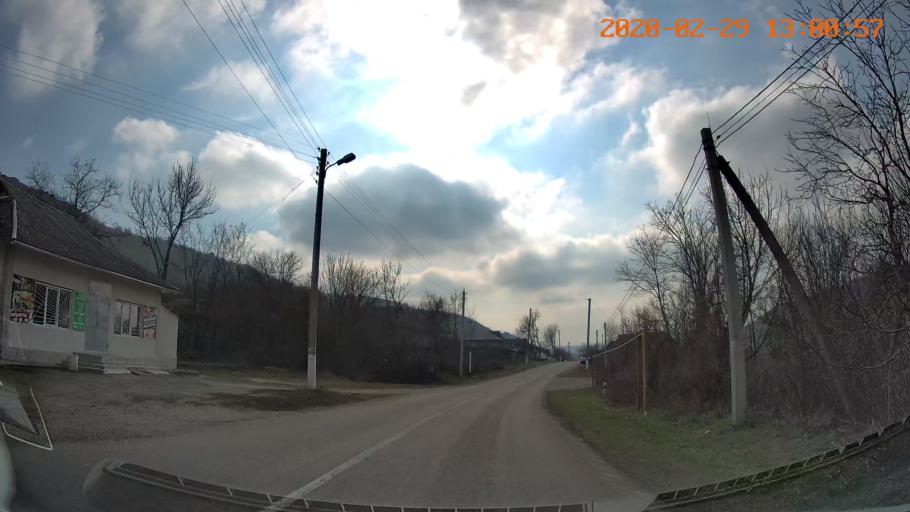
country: MD
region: Telenesti
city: Camenca
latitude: 48.0481
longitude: 28.7213
